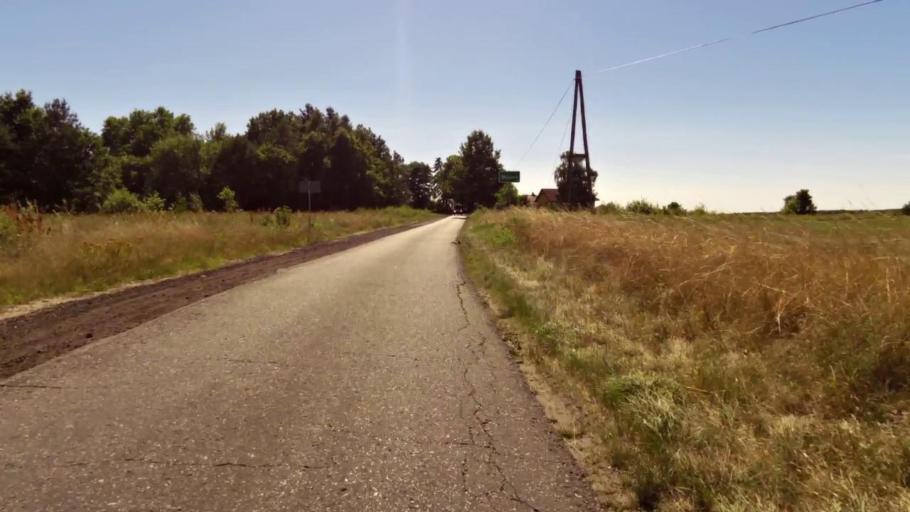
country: PL
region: West Pomeranian Voivodeship
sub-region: Powiat szczecinecki
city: Szczecinek
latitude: 53.6896
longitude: 16.6054
